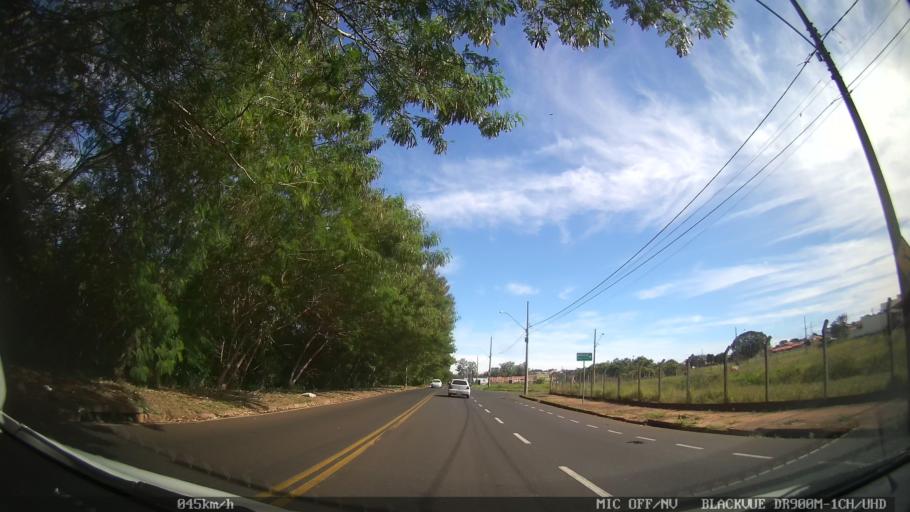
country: BR
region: Sao Paulo
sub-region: Sao Jose Do Rio Preto
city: Sao Jose do Rio Preto
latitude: -20.8424
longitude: -49.3548
